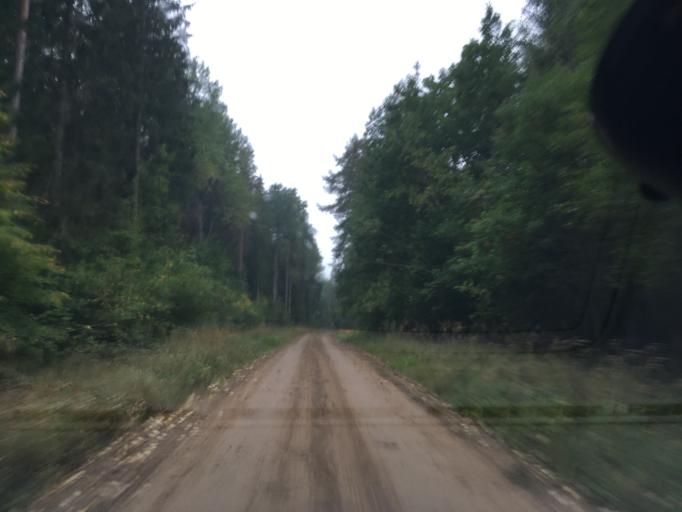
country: LV
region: Kuldigas Rajons
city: Kuldiga
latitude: 56.9840
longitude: 21.9912
